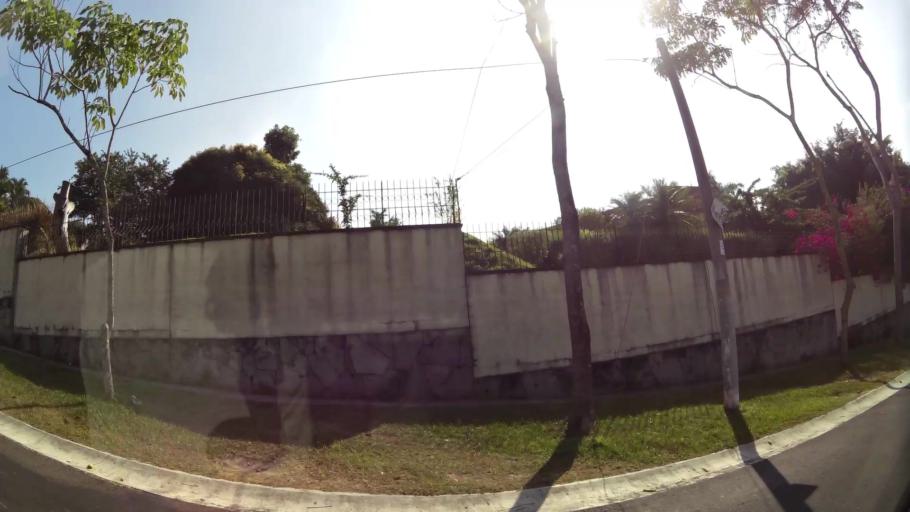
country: SV
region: La Libertad
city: Antiguo Cuscatlan
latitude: 13.6787
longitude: -89.2312
